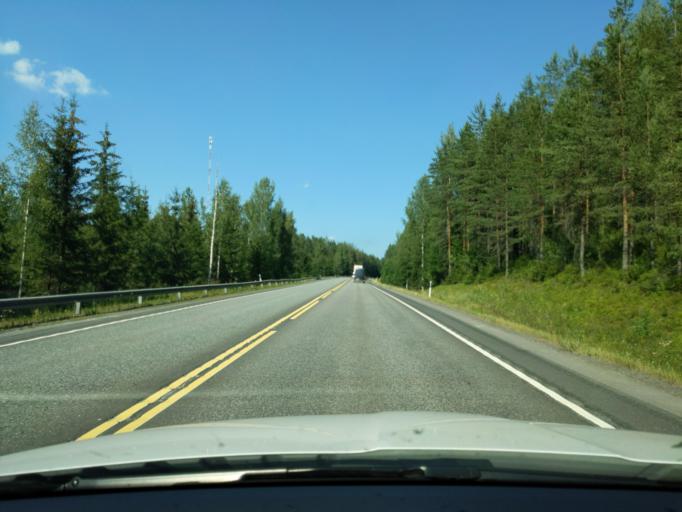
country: FI
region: Paijanne Tavastia
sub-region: Lahti
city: Hollola
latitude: 60.9545
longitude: 25.4354
